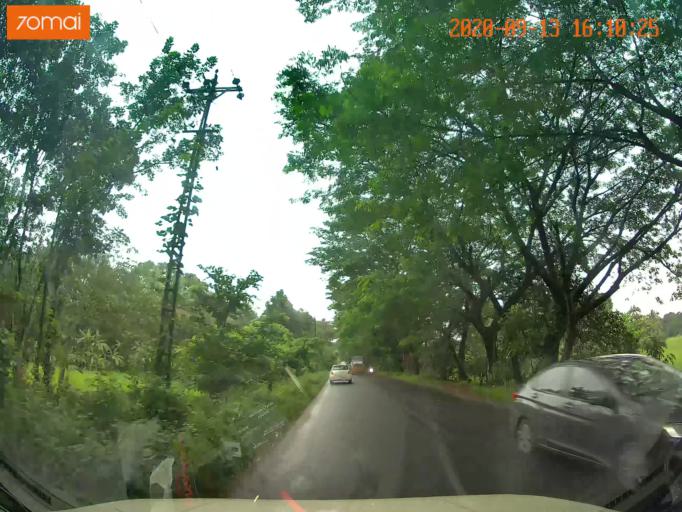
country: IN
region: Kerala
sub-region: Kottayam
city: Palackattumala
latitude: 9.6810
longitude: 76.6061
